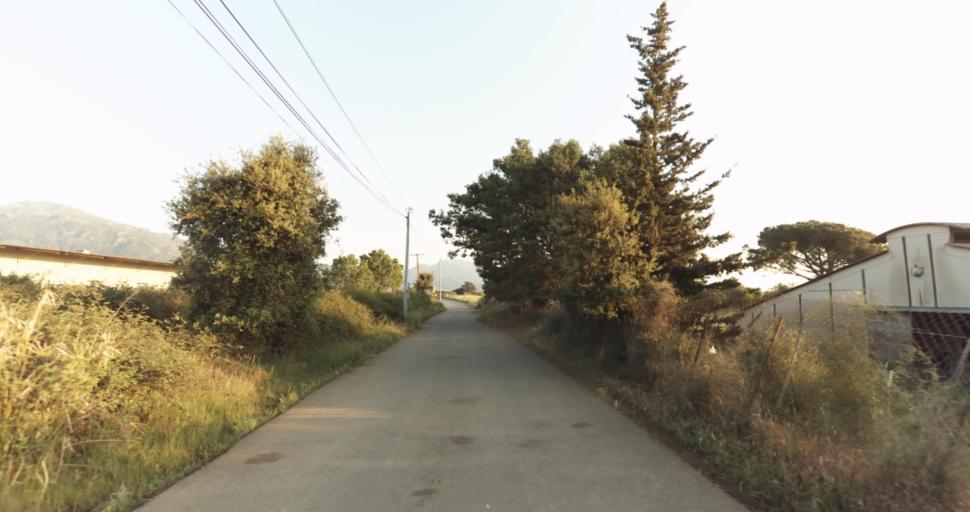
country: FR
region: Corsica
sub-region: Departement de la Haute-Corse
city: Biguglia
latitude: 42.6039
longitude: 9.4531
